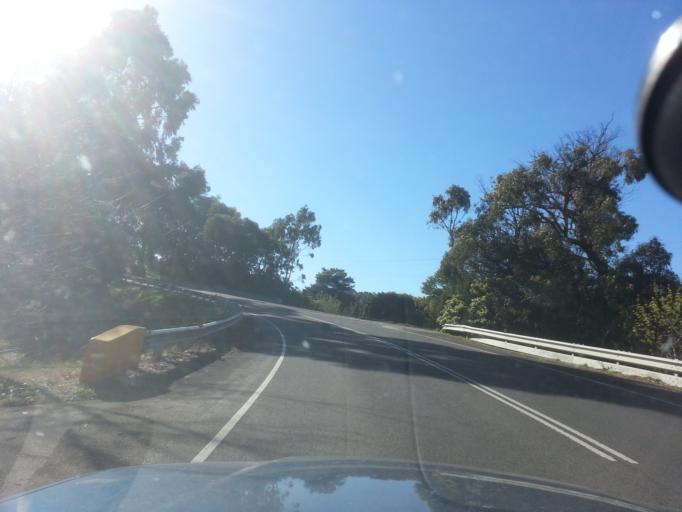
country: AU
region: Victoria
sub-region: Cardinia
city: Beaconsfield Upper
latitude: -38.0101
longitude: 145.4033
